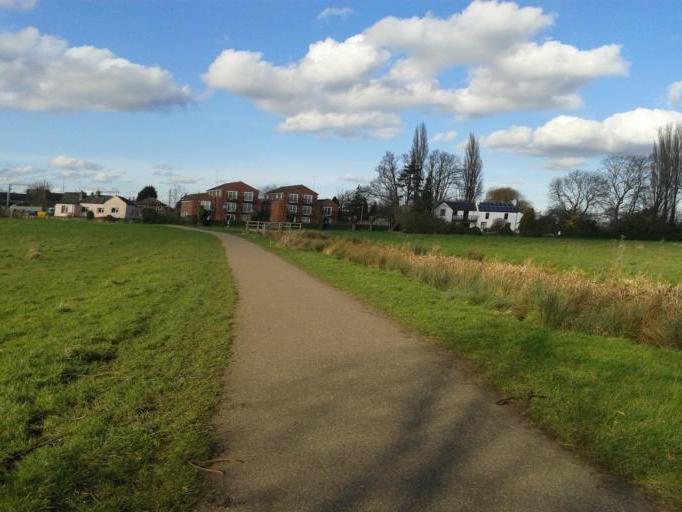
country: GB
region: England
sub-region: Cambridgeshire
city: Cambridge
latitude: 52.2193
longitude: 0.1590
